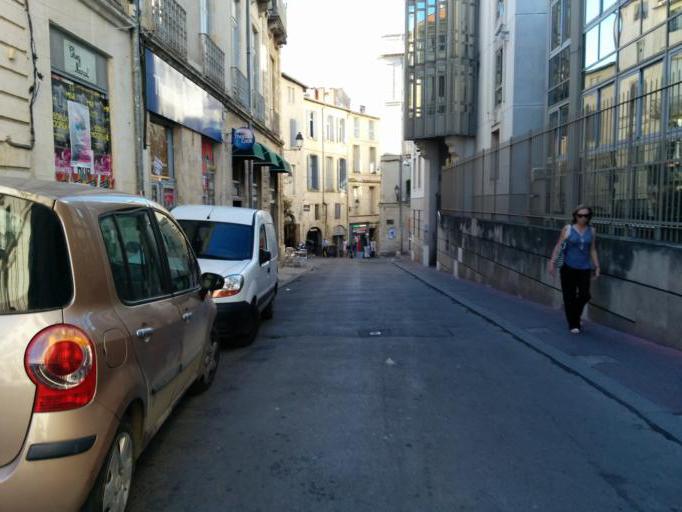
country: FR
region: Languedoc-Roussillon
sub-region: Departement de l'Herault
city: Montpellier
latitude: 43.6114
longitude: 3.8762
